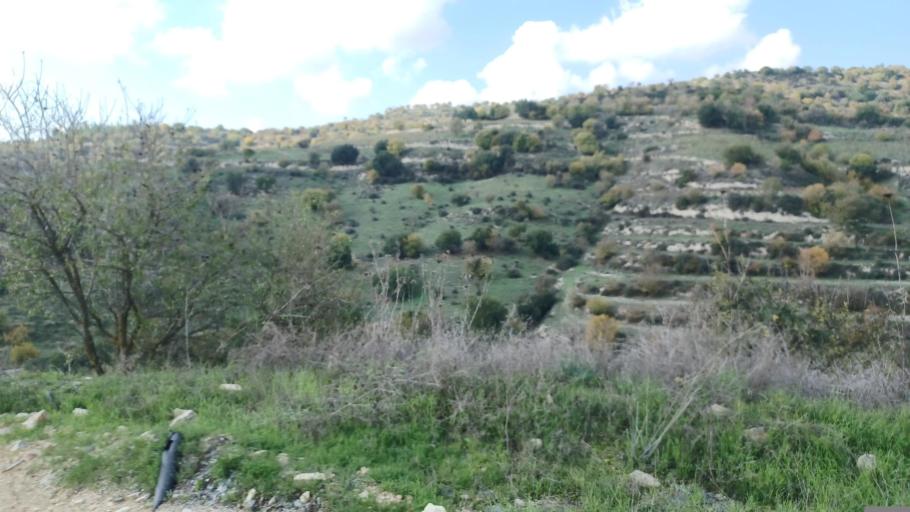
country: CY
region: Pafos
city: Mesogi
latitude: 34.8404
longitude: 32.5179
